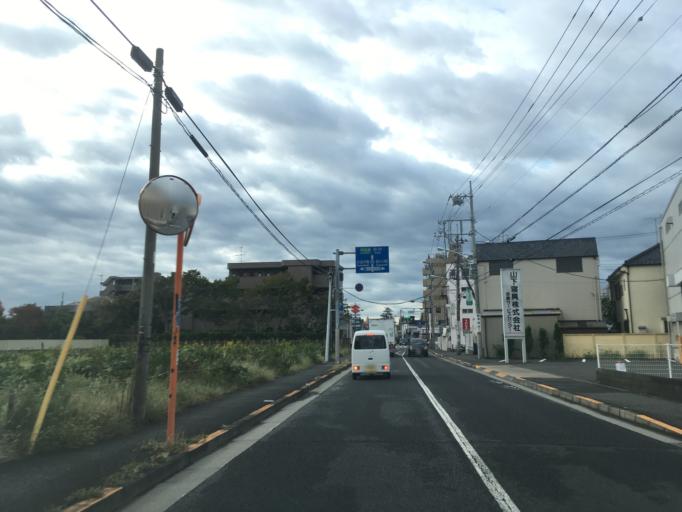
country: JP
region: Tokyo
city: Kokubunji
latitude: 35.7185
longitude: 139.4650
